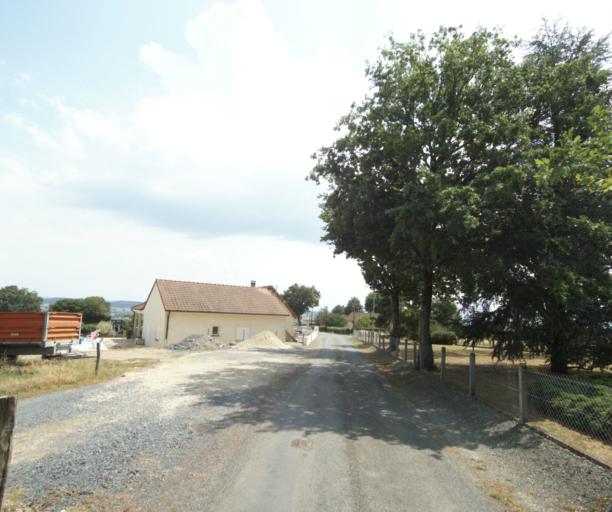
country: FR
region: Bourgogne
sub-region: Departement de Saone-et-Loire
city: Gueugnon
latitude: 46.6023
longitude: 4.0192
